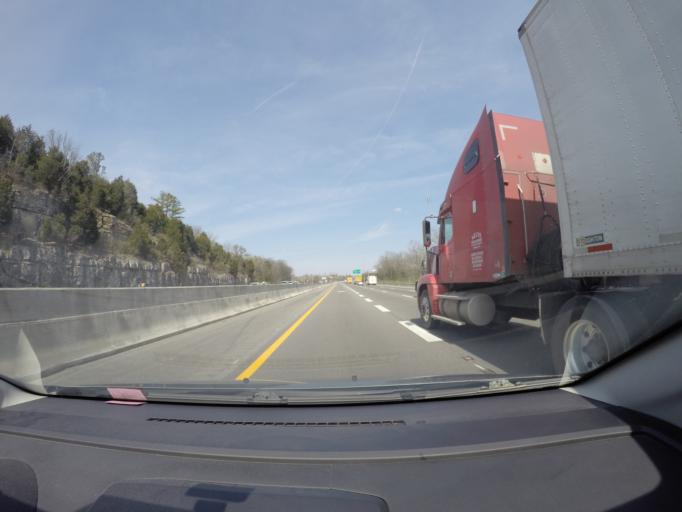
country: US
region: Tennessee
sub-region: Davidson County
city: Oak Hill
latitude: 36.0658
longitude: -86.6856
